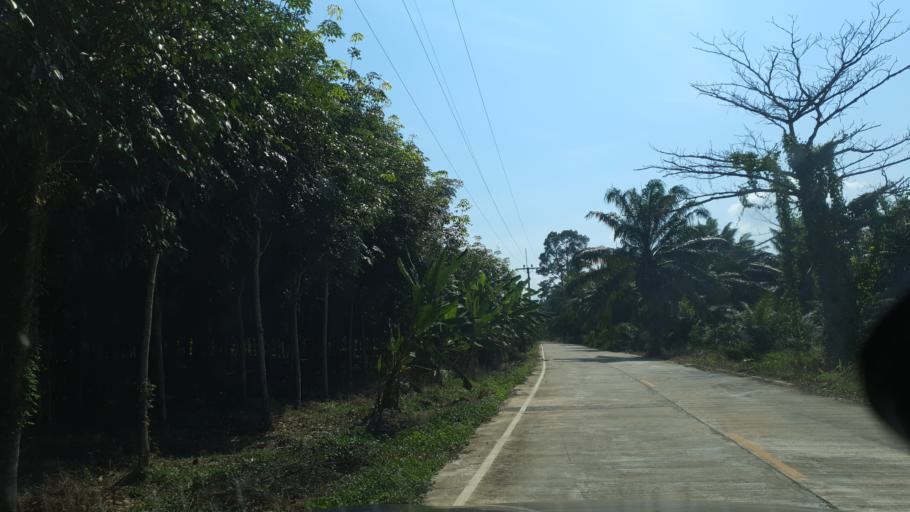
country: TH
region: Surat Thani
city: Tha Chana
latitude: 9.5916
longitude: 99.2021
